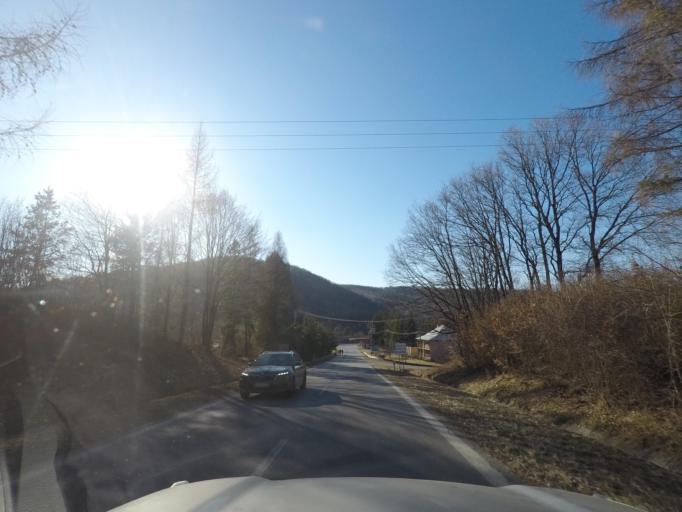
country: SK
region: Presovsky
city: Medzilaborce
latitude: 49.2529
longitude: 21.9142
